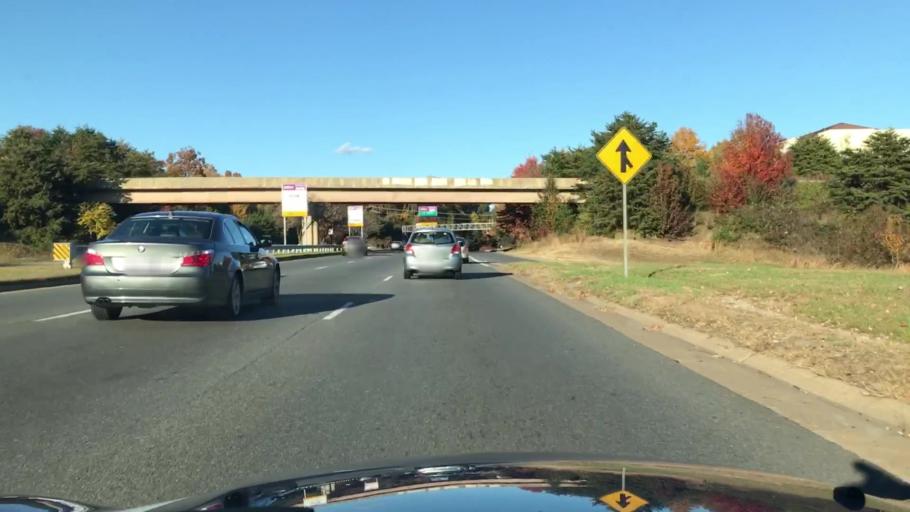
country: US
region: Virginia
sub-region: Prince William County
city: Potomac Mills
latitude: 38.6537
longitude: -77.2867
